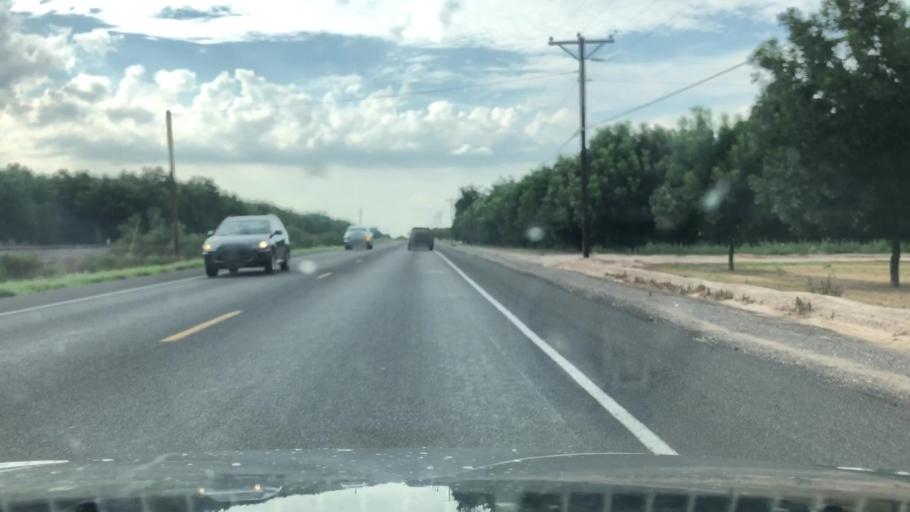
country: US
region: New Mexico
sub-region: Dona Ana County
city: Mesquite
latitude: 32.2157
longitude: -106.7288
